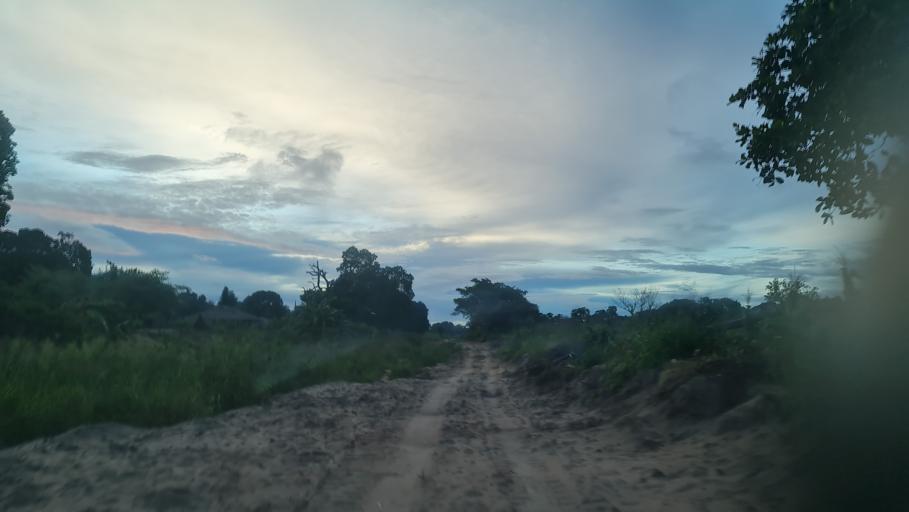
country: MZ
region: Nampula
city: Nampula
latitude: -14.7371
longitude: 39.9262
